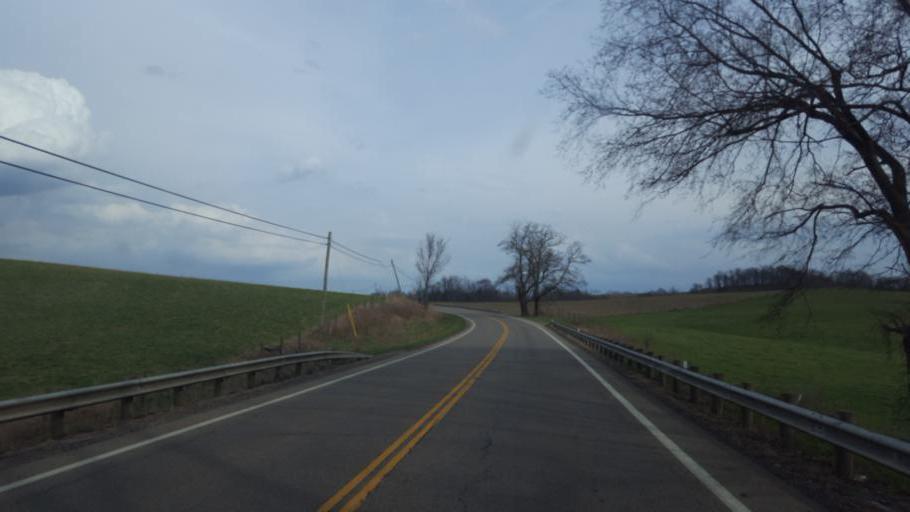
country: US
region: Ohio
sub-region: Coshocton County
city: Coshocton
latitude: 40.2326
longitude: -81.8494
